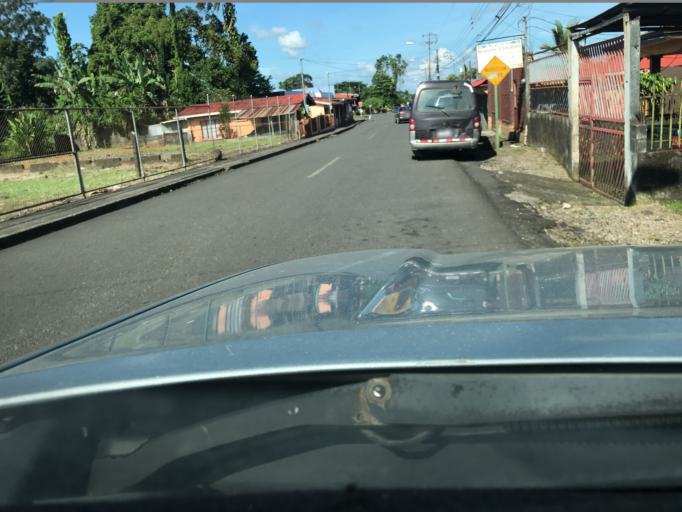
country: CR
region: Limon
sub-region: Canton de Guacimo
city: Guacimo
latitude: 10.2105
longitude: -83.6794
